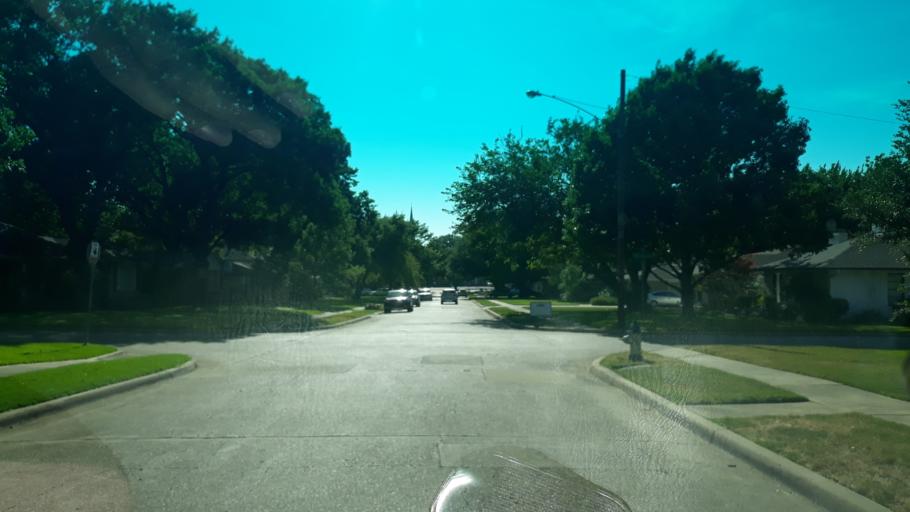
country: US
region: Texas
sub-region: Dallas County
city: Highland Park
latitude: 32.8256
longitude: -96.7578
